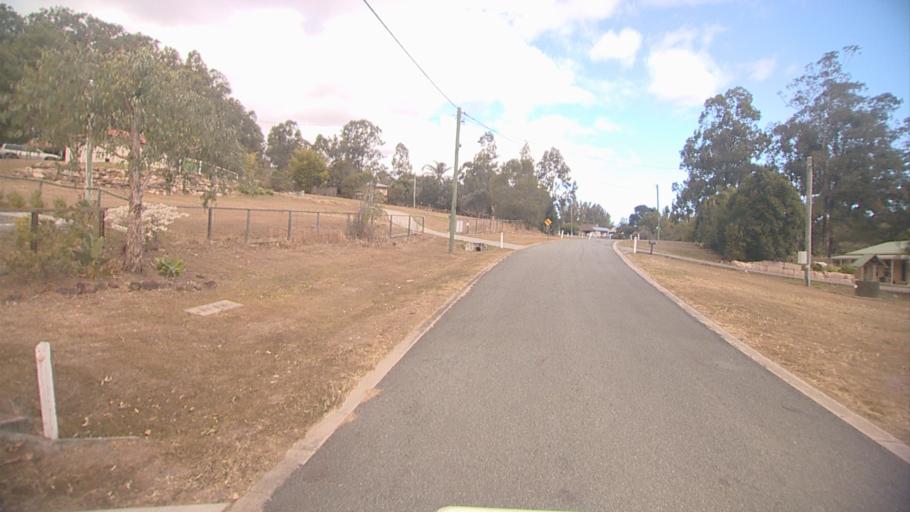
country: AU
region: Queensland
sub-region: Logan
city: Cedar Vale
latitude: -27.8850
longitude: 153.0136
